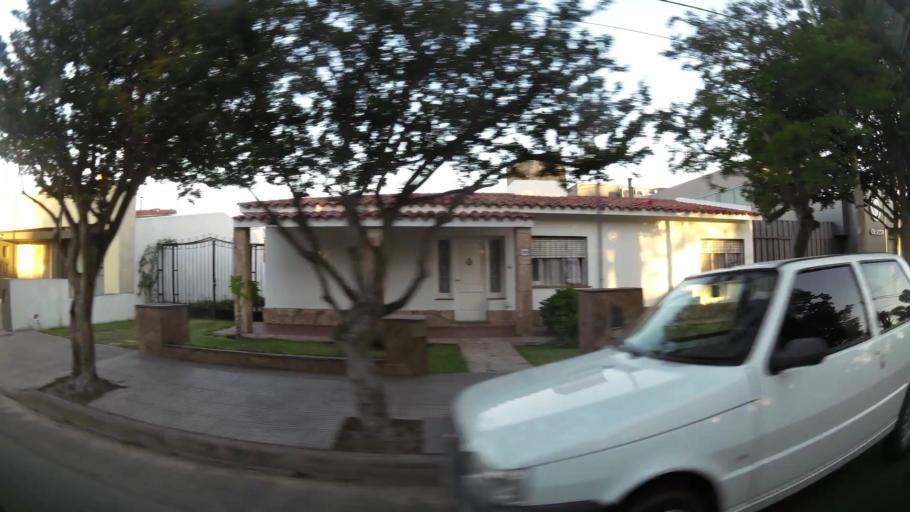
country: AR
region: Cordoba
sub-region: Departamento de Capital
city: Cordoba
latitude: -31.3760
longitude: -64.2227
